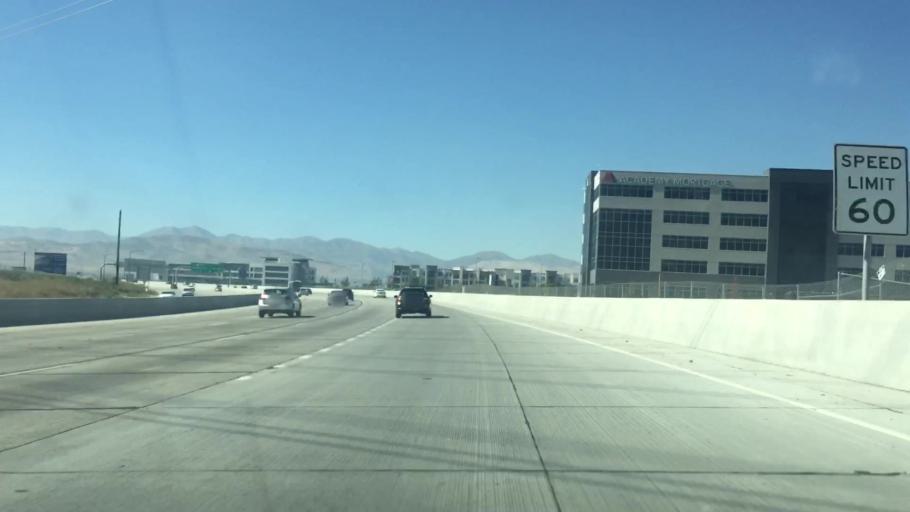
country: US
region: Utah
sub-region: Salt Lake County
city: Draper
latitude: 40.5045
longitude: -111.8995
